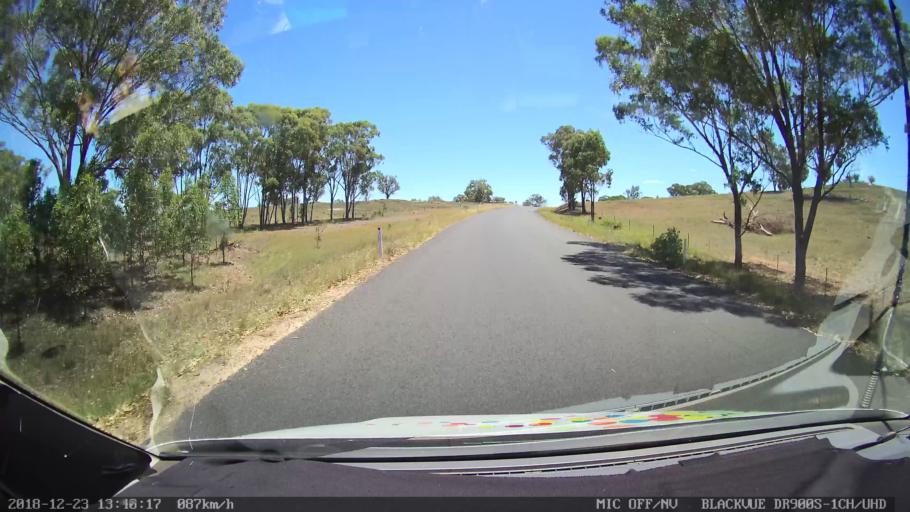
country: AU
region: New South Wales
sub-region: Armidale Dumaresq
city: Armidale
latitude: -30.4658
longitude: 151.1928
